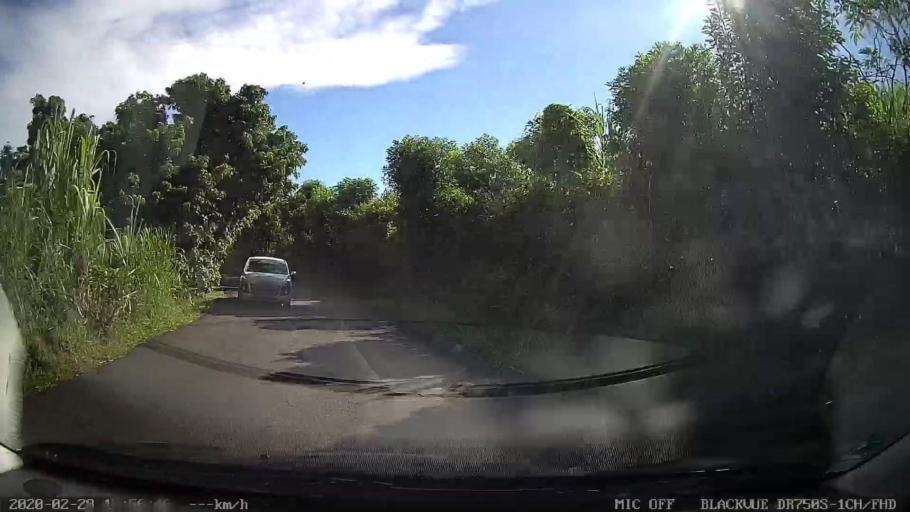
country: RE
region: Reunion
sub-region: Reunion
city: Sainte-Marie
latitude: -20.9383
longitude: 55.5254
